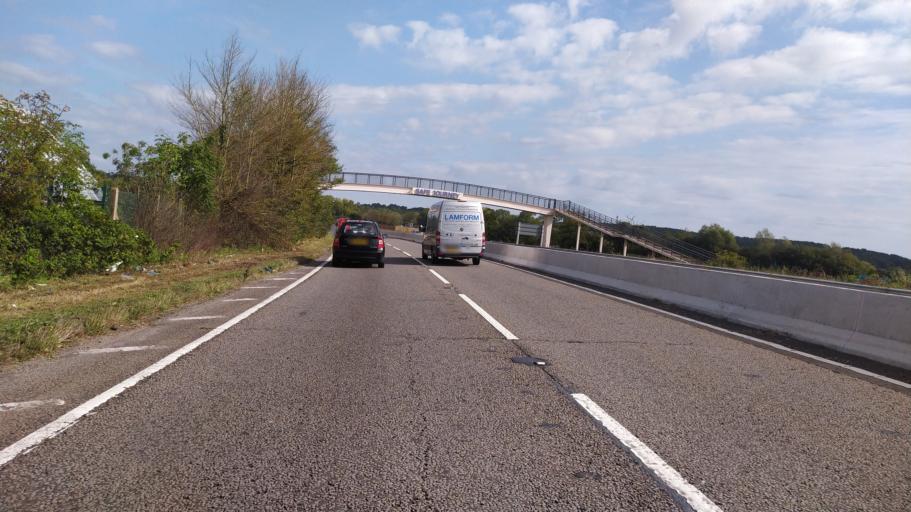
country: GB
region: England
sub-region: Dorset
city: Christchurch
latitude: 50.7519
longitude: -1.8198
